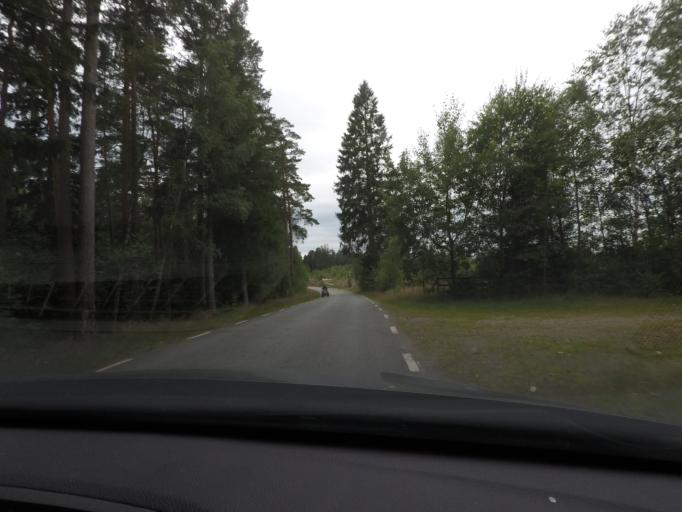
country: SE
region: Kronoberg
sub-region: Markaryds Kommun
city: Stromsnasbruk
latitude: 56.4250
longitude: 13.7497
